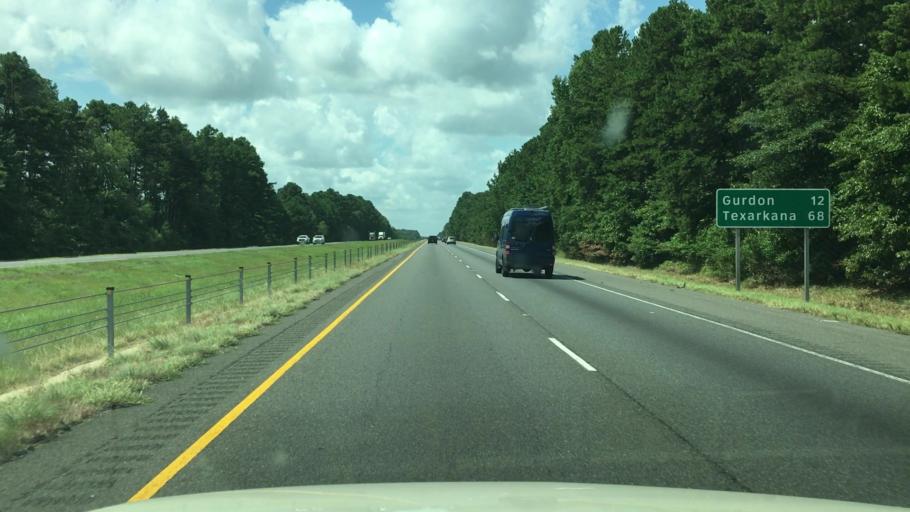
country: US
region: Arkansas
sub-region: Clark County
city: Arkadelphia
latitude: 34.0637
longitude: -93.1263
